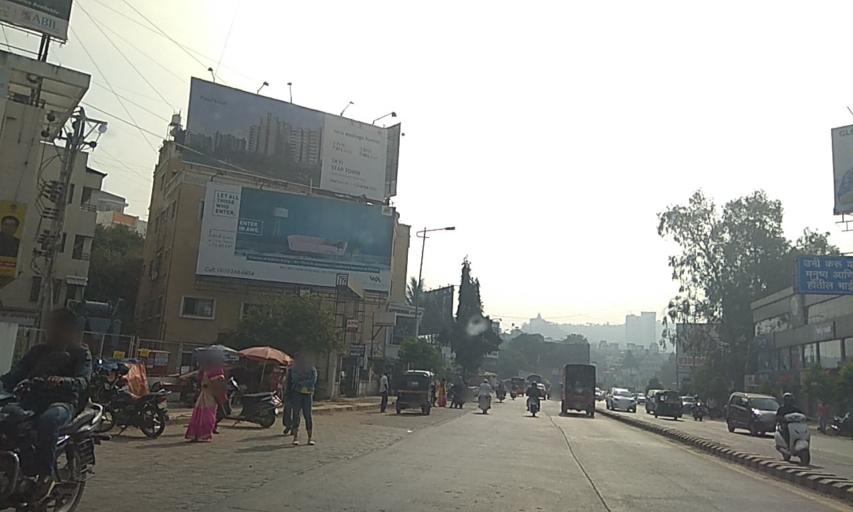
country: IN
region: Maharashtra
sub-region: Pune Division
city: Pimpri
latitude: 18.5634
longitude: 73.7830
